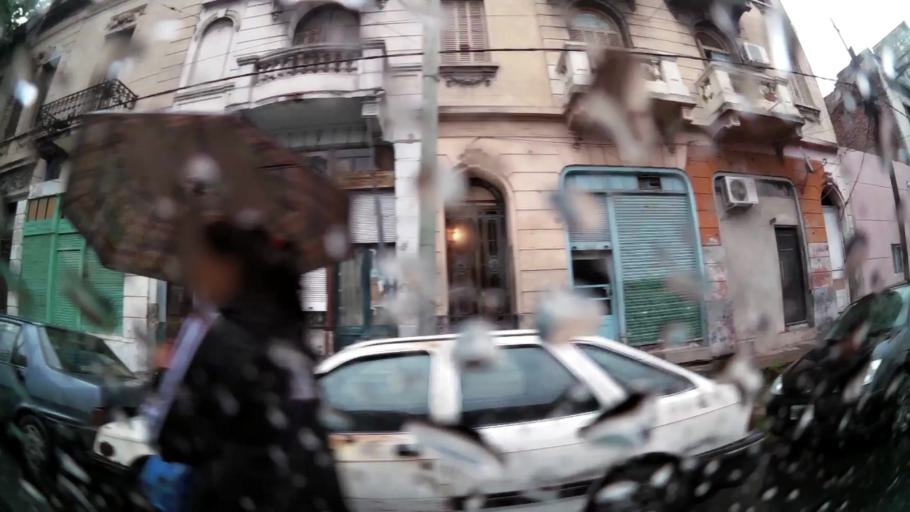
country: AR
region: Buenos Aires
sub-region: Partido de Avellaneda
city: Avellaneda
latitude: -34.6353
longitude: -58.3564
